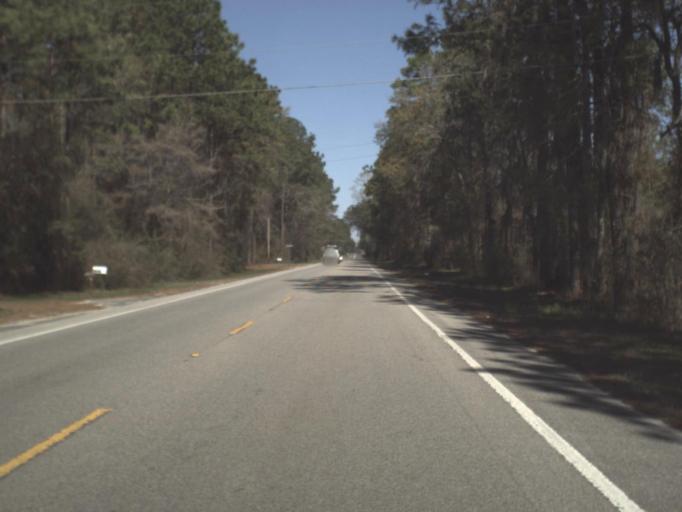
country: US
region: Florida
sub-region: Leon County
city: Woodville
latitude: 30.3111
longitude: -84.3118
